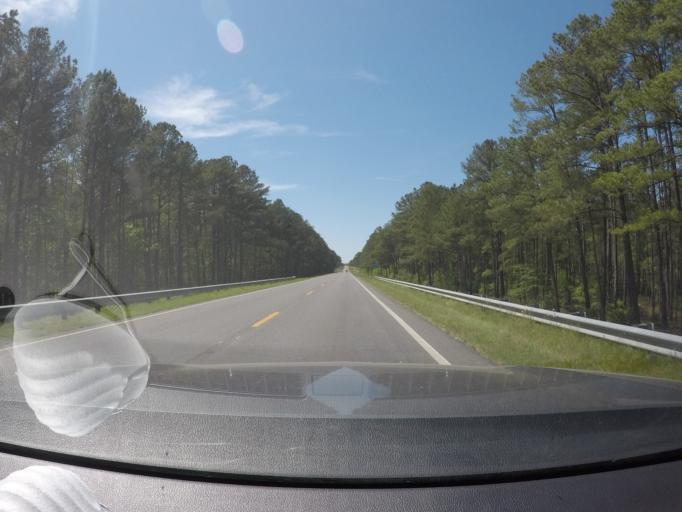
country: US
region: Georgia
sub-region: Evans County
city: Claxton
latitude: 32.1491
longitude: -81.7860
